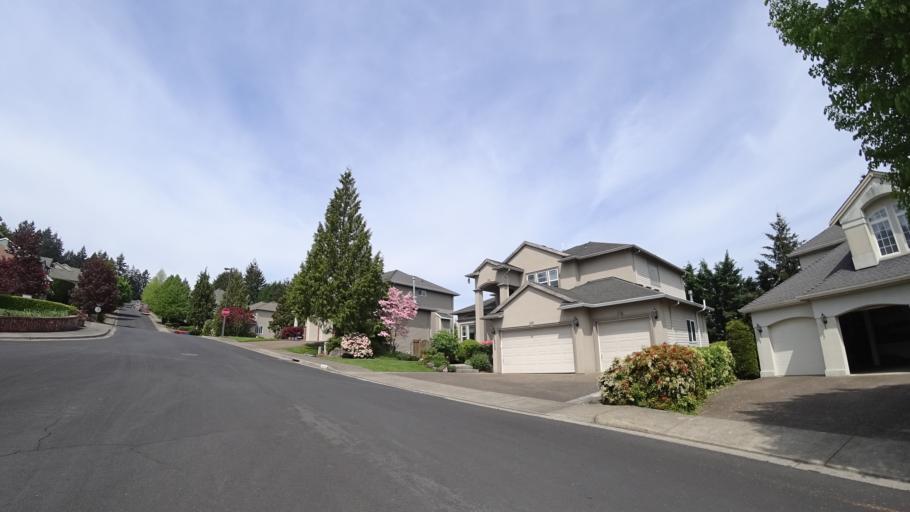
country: US
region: Oregon
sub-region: Washington County
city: Aloha
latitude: 45.4580
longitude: -122.8471
